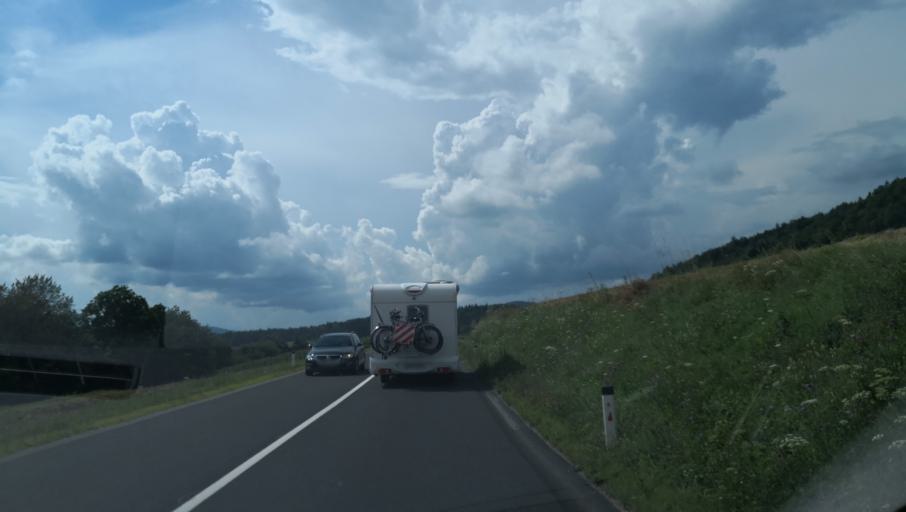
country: SI
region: Zuzemberk
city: Zuzemberk
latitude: 45.8383
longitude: 14.9156
